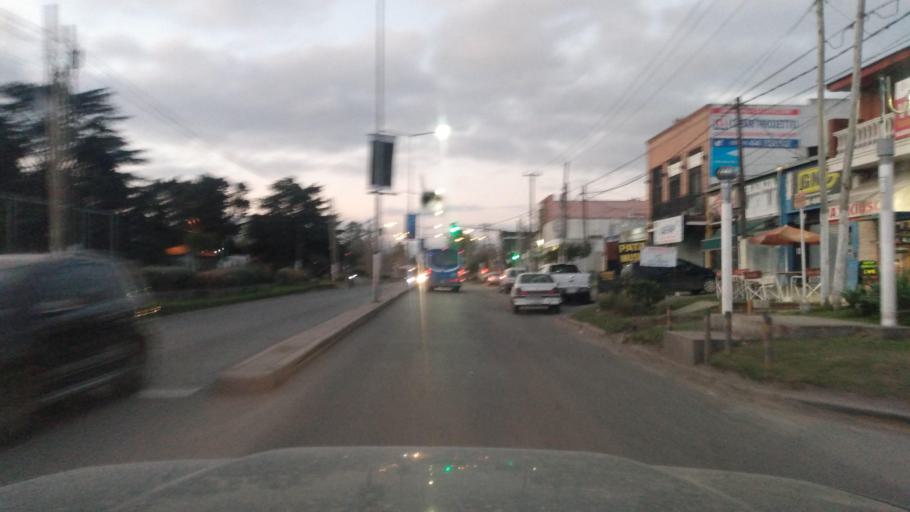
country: AR
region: Buenos Aires
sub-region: Partido de Pilar
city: Pilar
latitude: -34.4518
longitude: -58.9073
